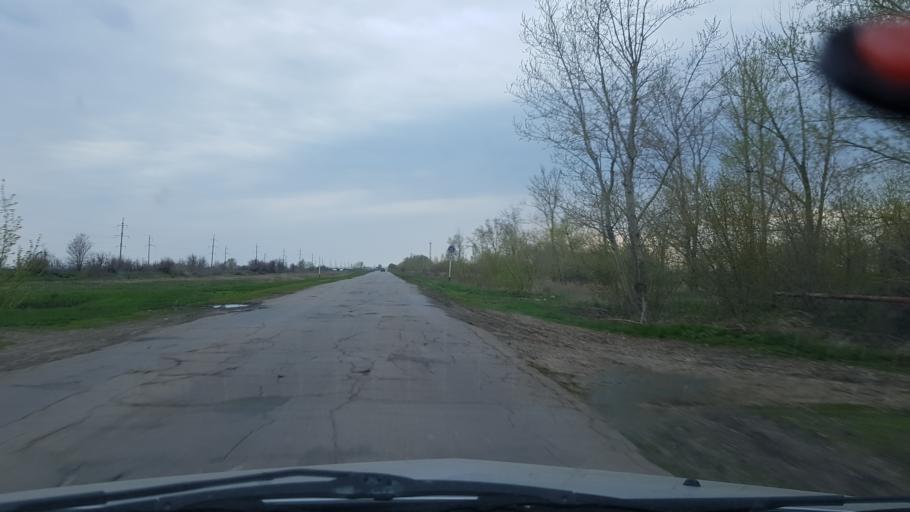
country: RU
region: Samara
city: Khryashchevka
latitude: 53.6685
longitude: 49.1375
